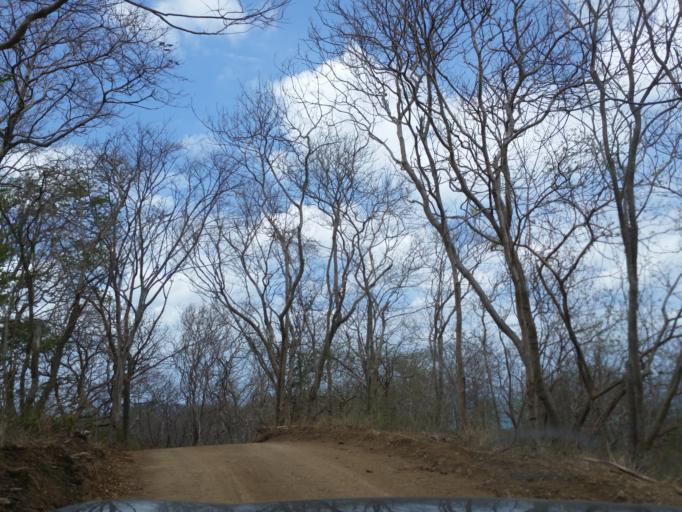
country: NI
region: Rivas
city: Tola
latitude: 11.4238
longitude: -86.0680
